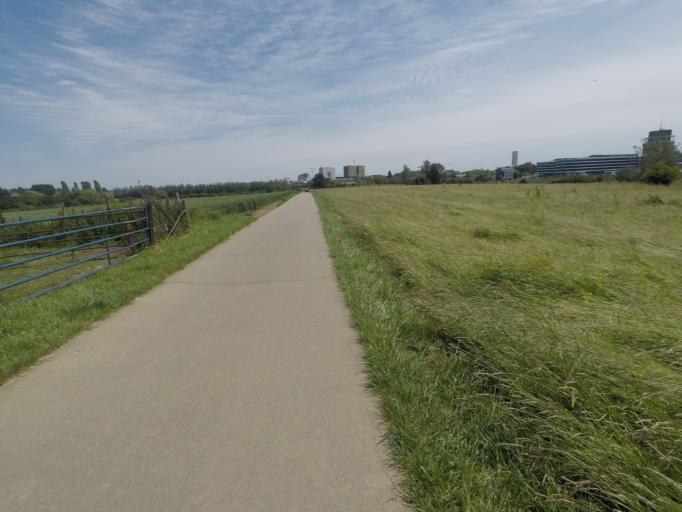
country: LU
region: Luxembourg
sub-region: Canton de Luxembourg
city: Luxembourg
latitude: 49.5824
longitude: 6.1044
